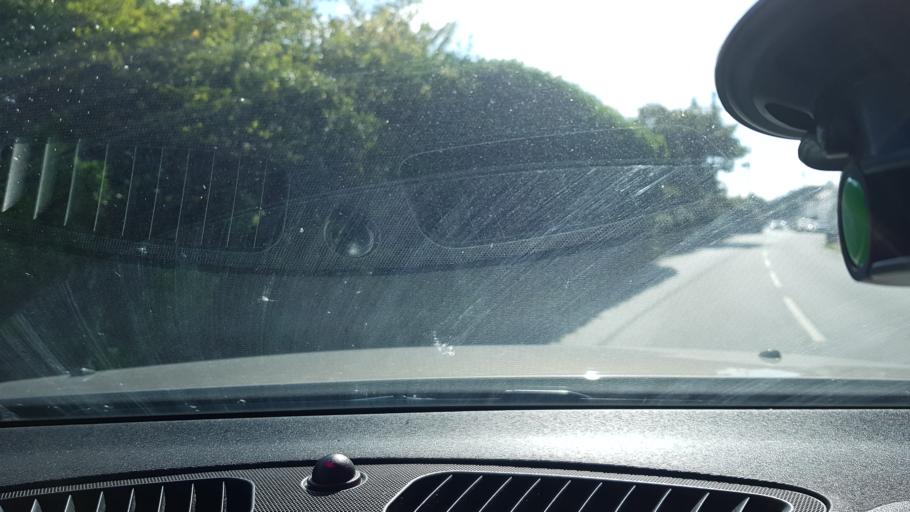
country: GB
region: England
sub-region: Cornwall
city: Tintagel
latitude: 50.6674
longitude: -4.7374
